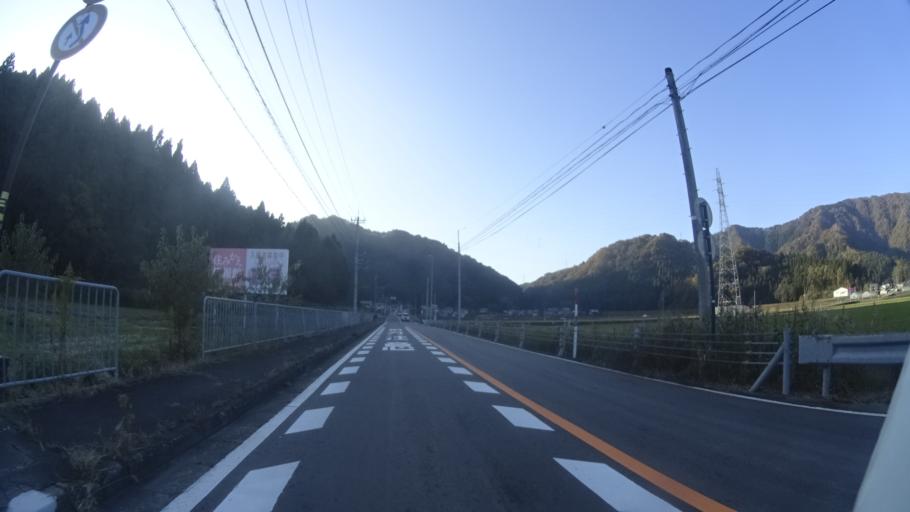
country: JP
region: Fukui
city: Ono
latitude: 35.9946
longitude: 136.4639
